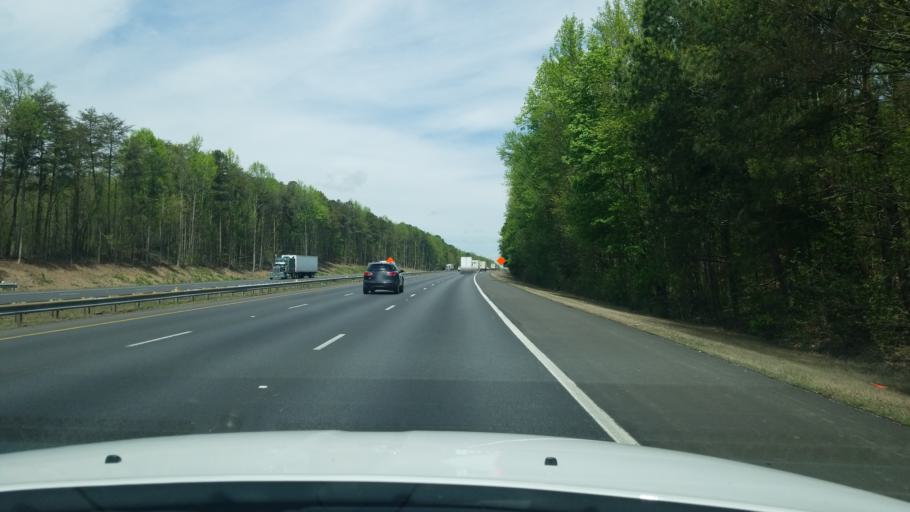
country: US
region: Georgia
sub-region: Whitfield County
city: Dalton
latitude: 34.7070
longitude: -85.0070
